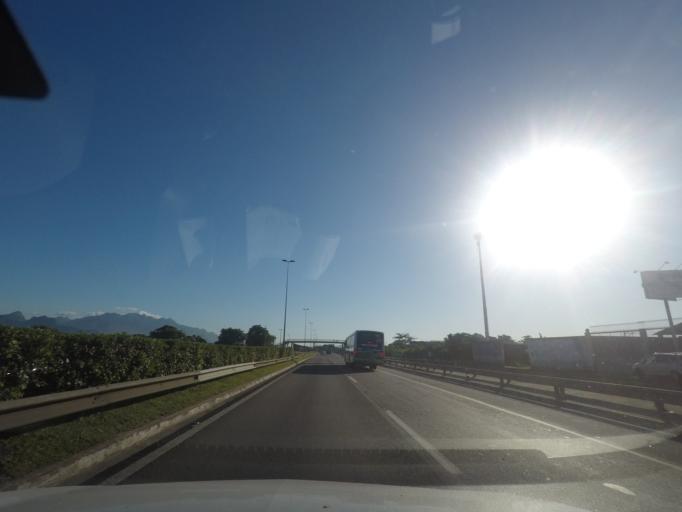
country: BR
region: Rio de Janeiro
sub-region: Duque De Caxias
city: Duque de Caxias
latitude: -22.6684
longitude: -43.2684
